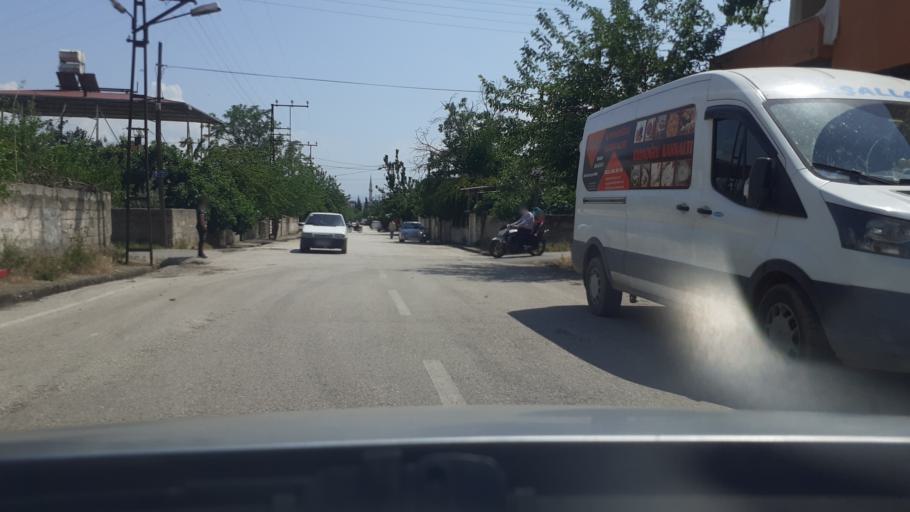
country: TR
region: Hatay
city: Kirikhan
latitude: 36.4915
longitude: 36.3540
